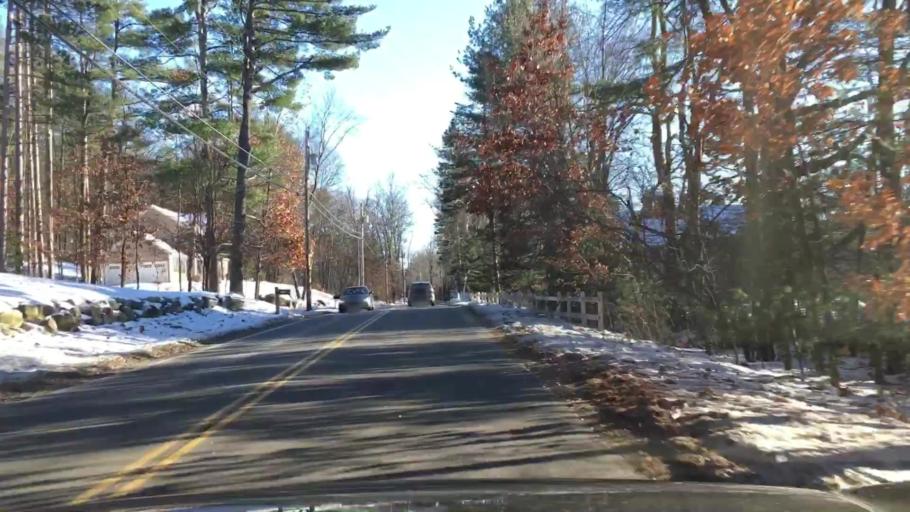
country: US
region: New Hampshire
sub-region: Hillsborough County
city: Milford
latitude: 42.8336
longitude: -71.5924
